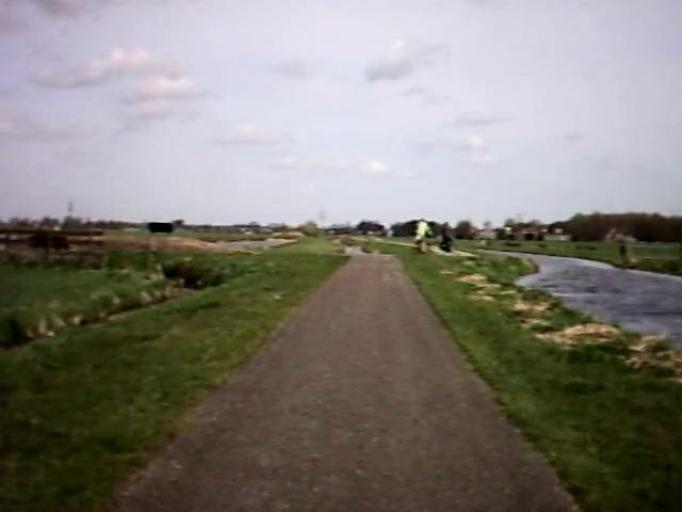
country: NL
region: Utrecht
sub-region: Gemeente De Bilt
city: De Bilt
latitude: 52.1336
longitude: 5.1477
